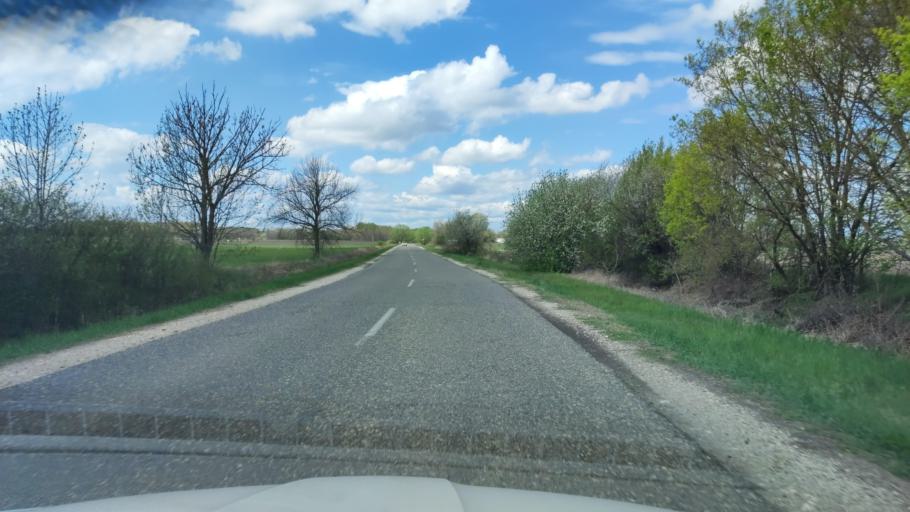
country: HU
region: Pest
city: Tortel
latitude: 47.1327
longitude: 19.9101
